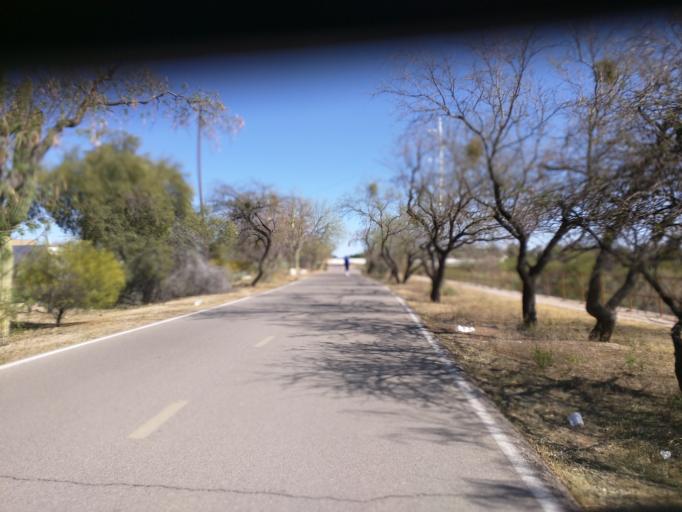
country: US
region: Arizona
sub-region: Pima County
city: Flowing Wells
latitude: 32.2913
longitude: -110.9719
